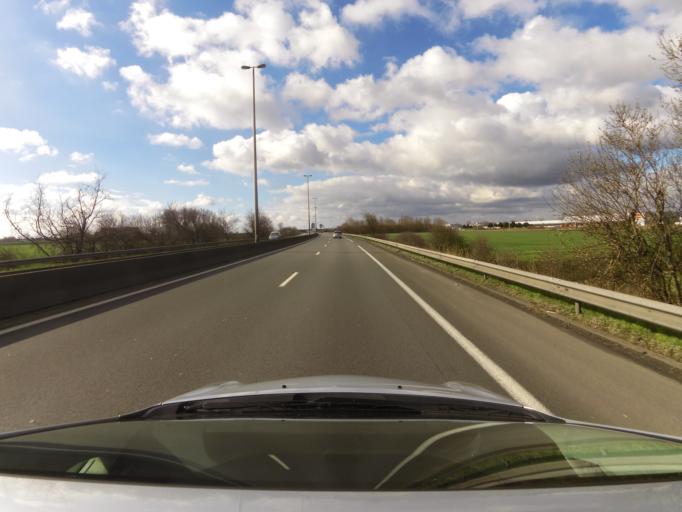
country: FR
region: Nord-Pas-de-Calais
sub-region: Departement du Nord
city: Loon-Plage
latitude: 50.9804
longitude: 2.2254
